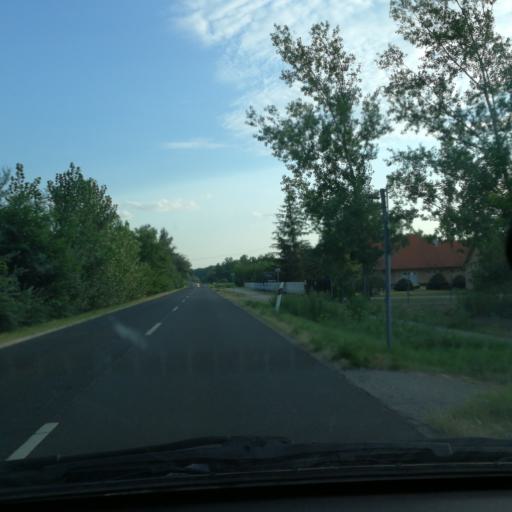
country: HU
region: Bacs-Kiskun
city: Jaszszentlaszlo
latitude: 46.5499
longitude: 19.7462
